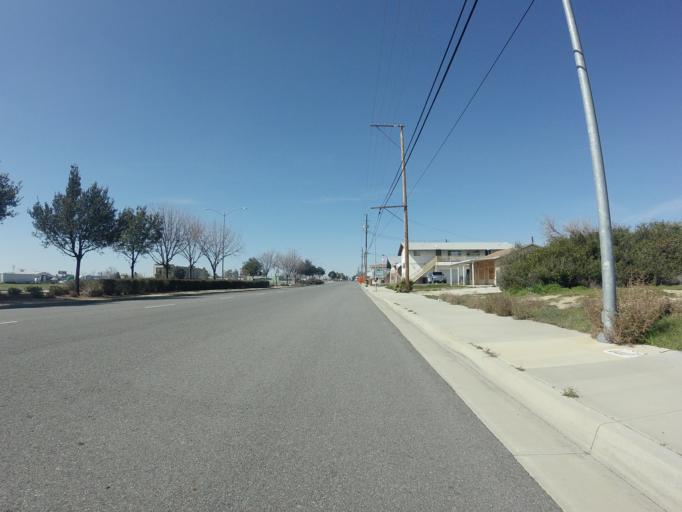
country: US
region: California
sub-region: Riverside County
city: Beaumont
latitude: 33.9293
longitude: -116.9397
